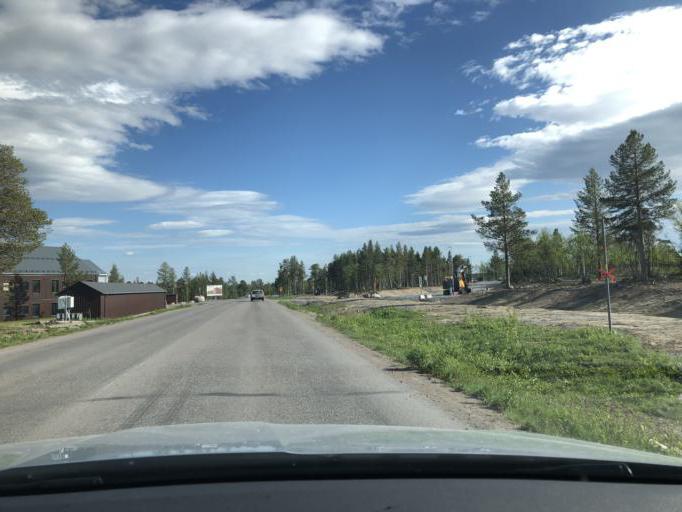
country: SE
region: Norrbotten
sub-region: Kiruna Kommun
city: Kiruna
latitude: 67.8533
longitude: 20.2751
